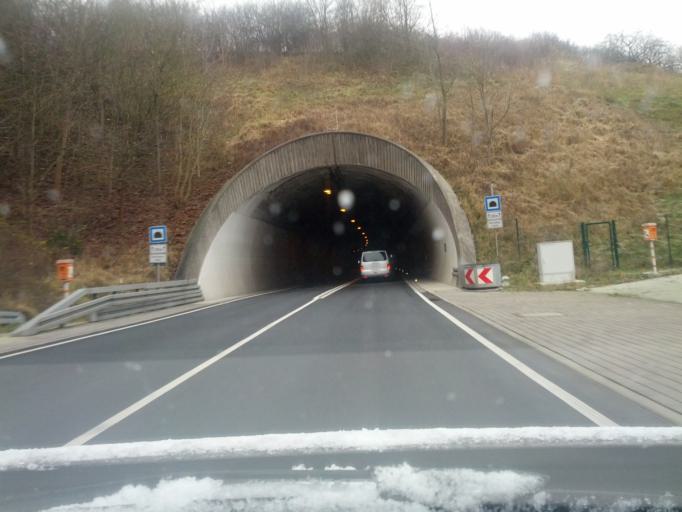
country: DE
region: Thuringia
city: Lindewerra
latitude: 51.3074
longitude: 9.9367
